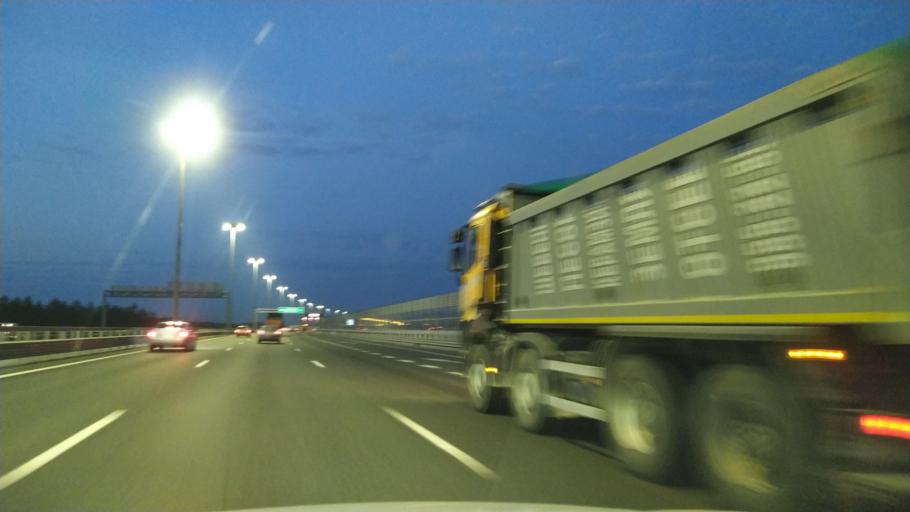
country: RU
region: St.-Petersburg
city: Pargolovo
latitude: 60.0992
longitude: 30.2843
